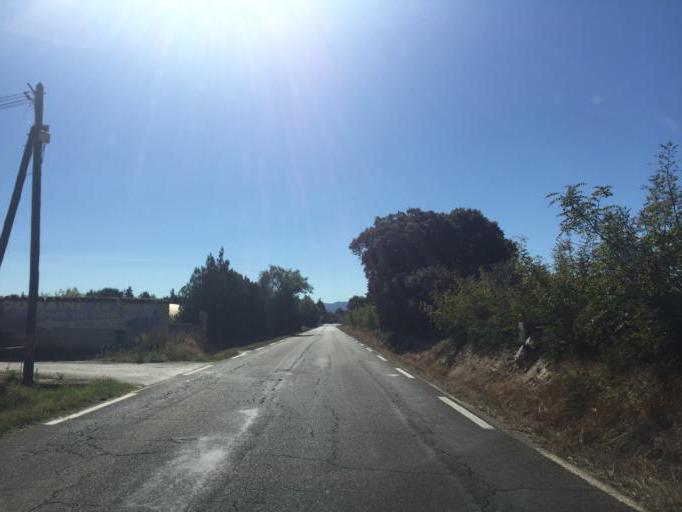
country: FR
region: Provence-Alpes-Cote d'Azur
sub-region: Departement du Vaucluse
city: Carpentras
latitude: 44.0311
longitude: 5.0809
